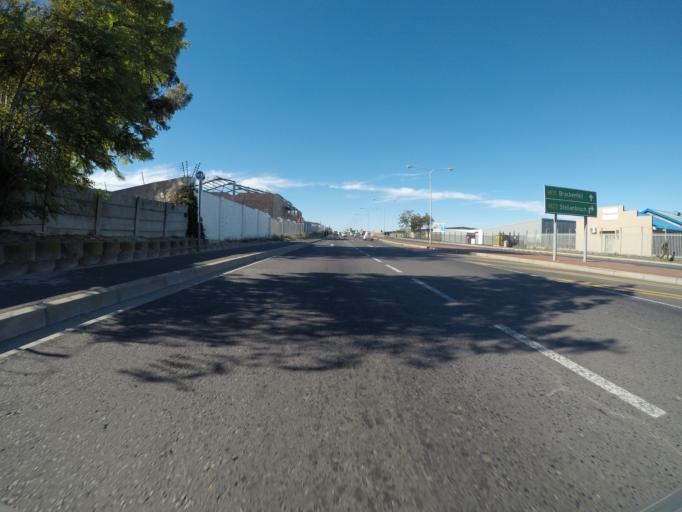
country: ZA
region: Western Cape
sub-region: City of Cape Town
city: Kraaifontein
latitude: -33.9074
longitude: 18.6667
